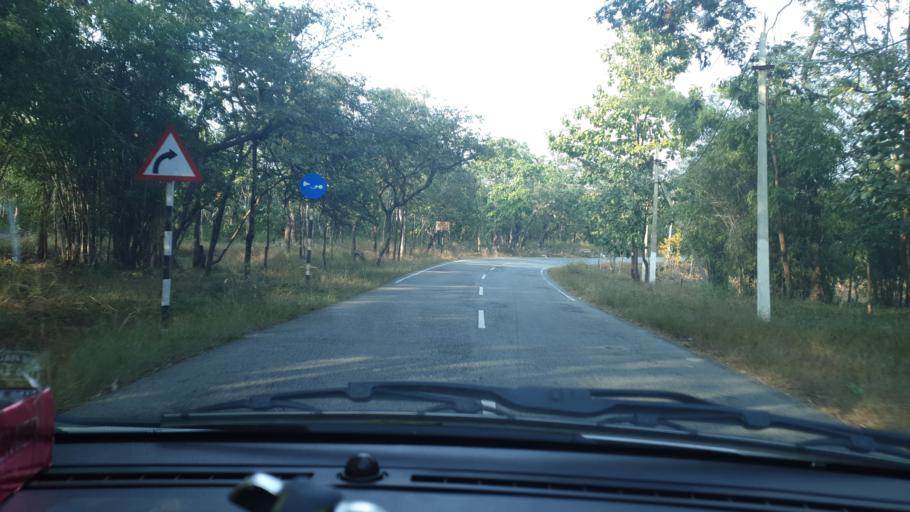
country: IN
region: Andhra Pradesh
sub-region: Kurnool
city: Srisailam
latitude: 16.3053
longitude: 78.7324
